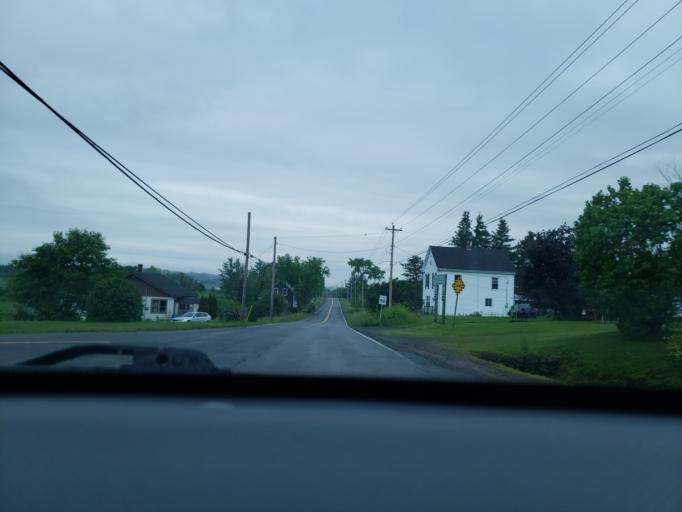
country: CA
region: Nova Scotia
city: Windsor
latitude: 45.0572
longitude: -64.0019
